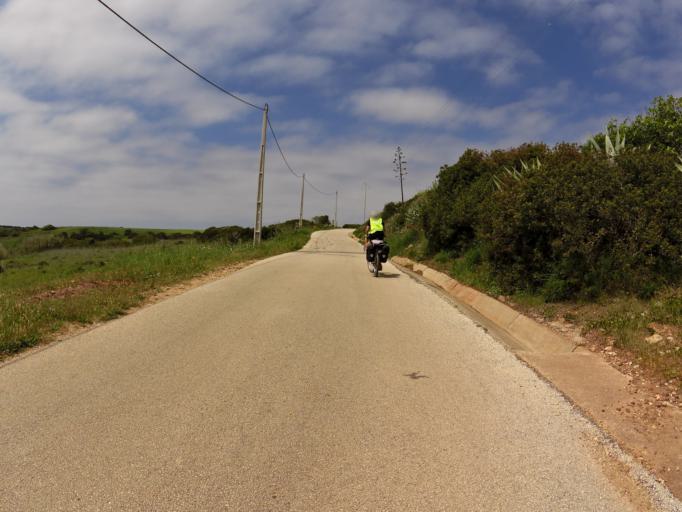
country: PT
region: Faro
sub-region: Vila do Bispo
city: Vila do Bispo
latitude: 37.0666
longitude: -8.8634
